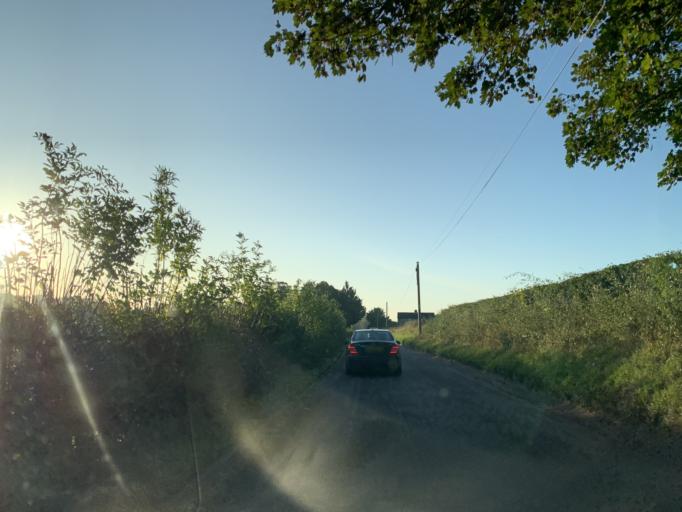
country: GB
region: England
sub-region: Wiltshire
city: Woodford
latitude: 51.1022
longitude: -1.8262
